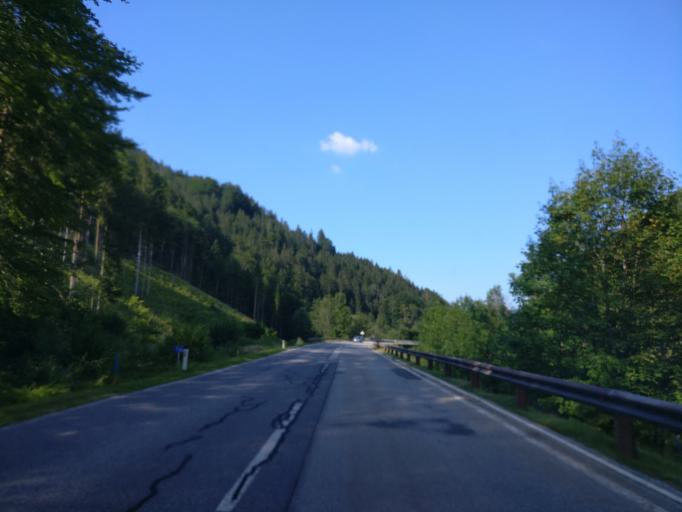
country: AT
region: Styria
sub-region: Politischer Bezirk Liezen
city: Palfau
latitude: 47.7314
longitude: 14.8681
